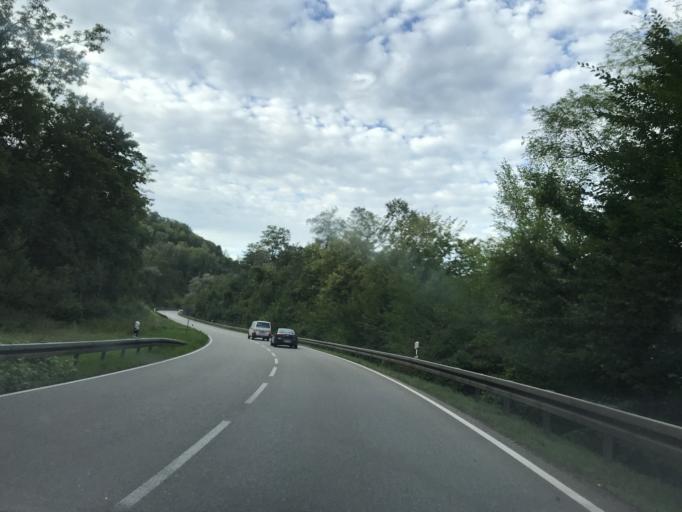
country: DE
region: Baden-Wuerttemberg
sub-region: Freiburg Region
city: Schworstadt
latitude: 47.5869
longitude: 7.9102
